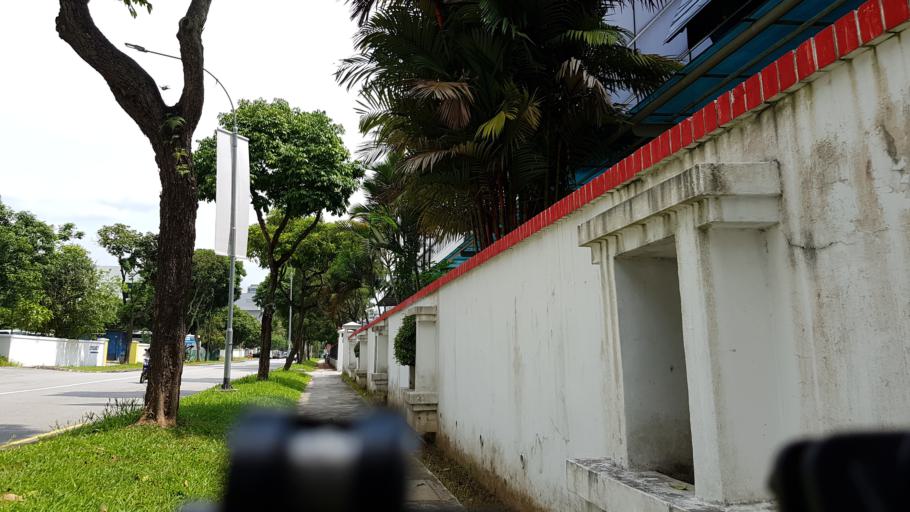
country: MY
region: Johor
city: Kampung Pasir Gudang Baru
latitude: 1.4415
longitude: 103.8357
